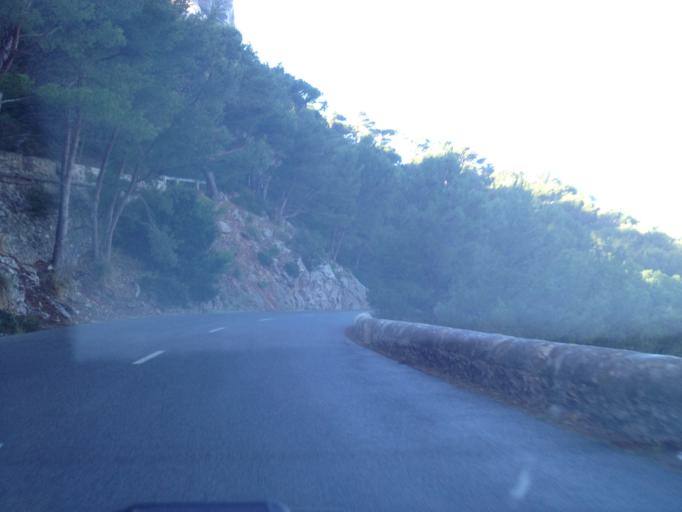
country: ES
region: Balearic Islands
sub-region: Illes Balears
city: Alcudia
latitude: 39.9305
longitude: 3.1246
